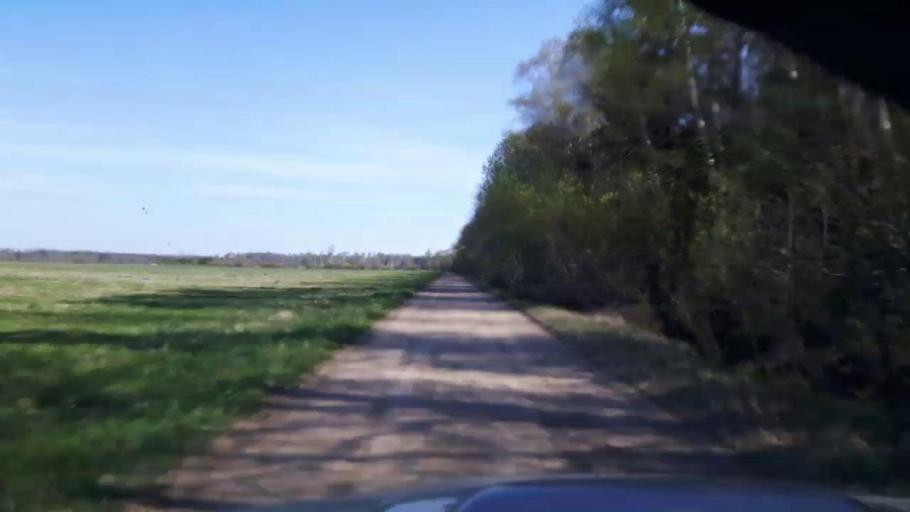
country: EE
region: Paernumaa
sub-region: Tootsi vald
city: Tootsi
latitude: 58.4824
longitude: 24.9275
